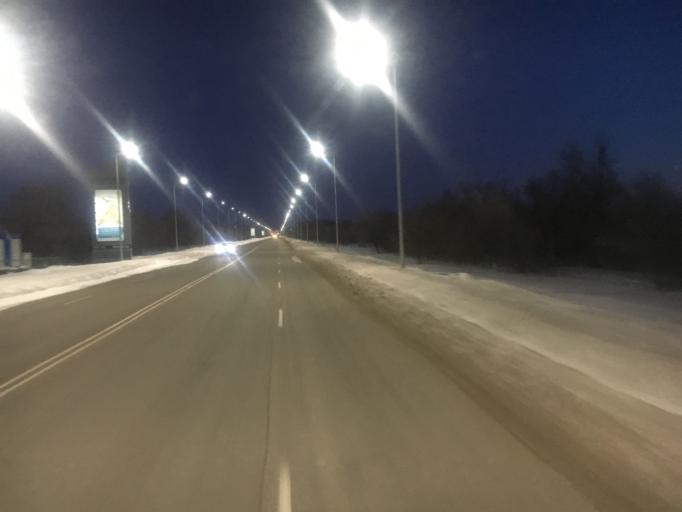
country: KZ
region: Batys Qazaqstan
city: Oral
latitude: 51.1609
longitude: 51.5292
